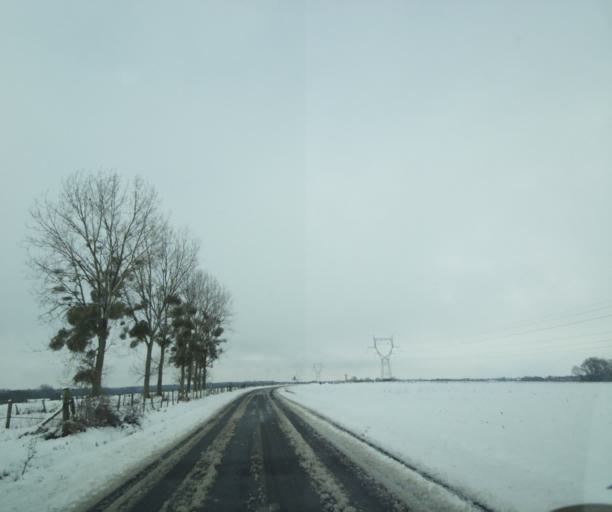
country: FR
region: Champagne-Ardenne
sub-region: Departement de la Haute-Marne
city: Montier-en-Der
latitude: 48.5075
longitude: 4.7246
